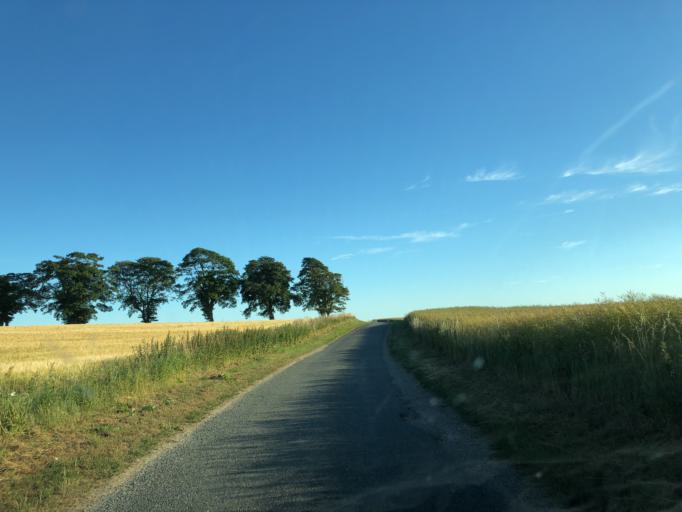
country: DK
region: Central Jutland
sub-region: Horsens Kommune
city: Horsens
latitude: 55.9019
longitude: 9.8624
